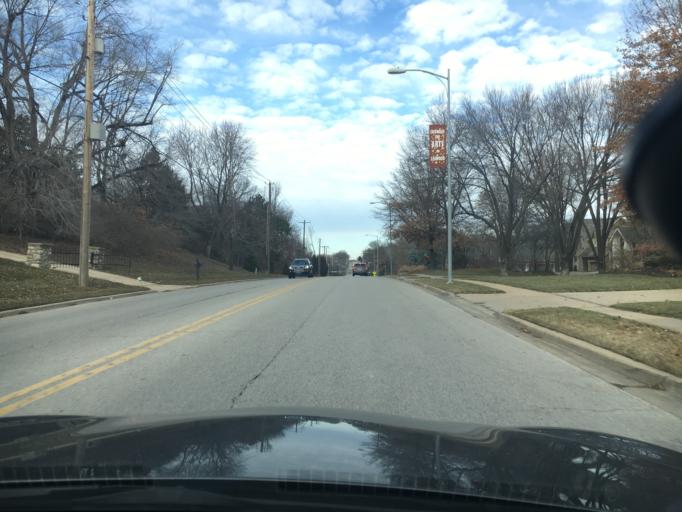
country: US
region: Kansas
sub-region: Johnson County
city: Leawood
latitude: 38.9034
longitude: -94.6305
